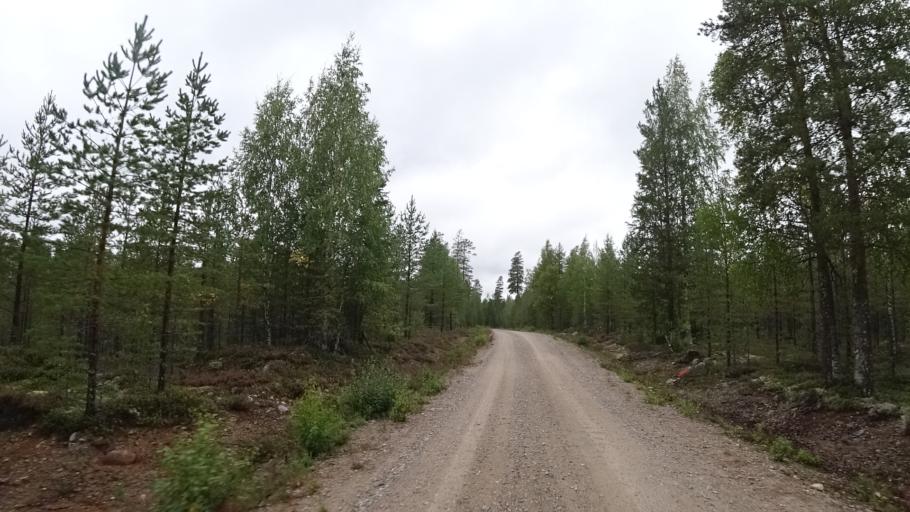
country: FI
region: North Karelia
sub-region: Pielisen Karjala
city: Lieksa
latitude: 63.5073
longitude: 30.1445
